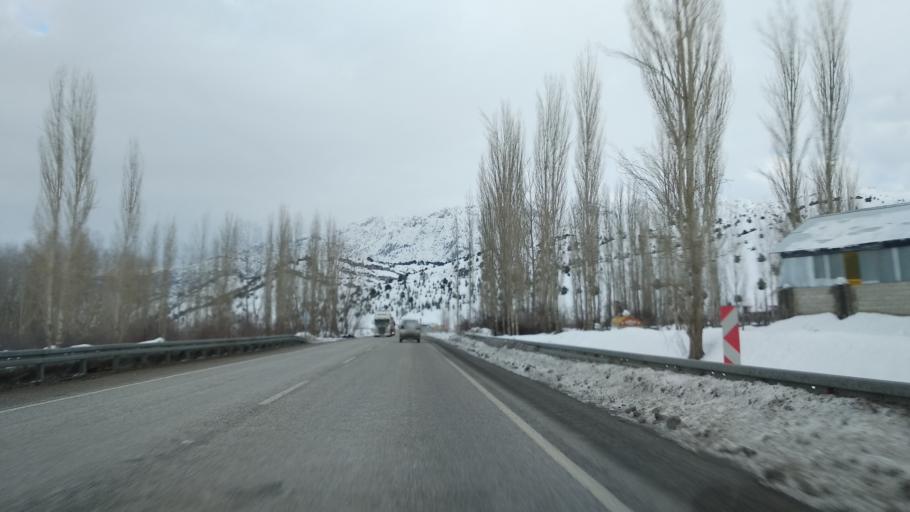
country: TR
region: Kahramanmaras
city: Goksun
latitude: 37.9974
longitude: 36.5267
